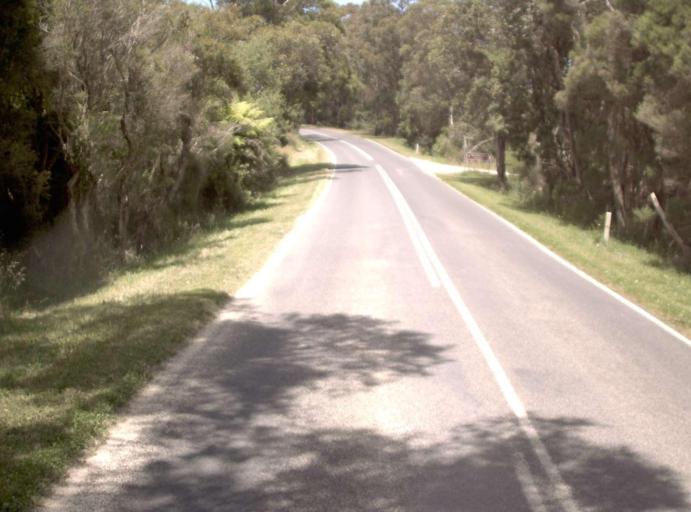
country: AU
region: Victoria
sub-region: Bass Coast
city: North Wonthaggi
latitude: -38.7289
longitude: 146.1217
